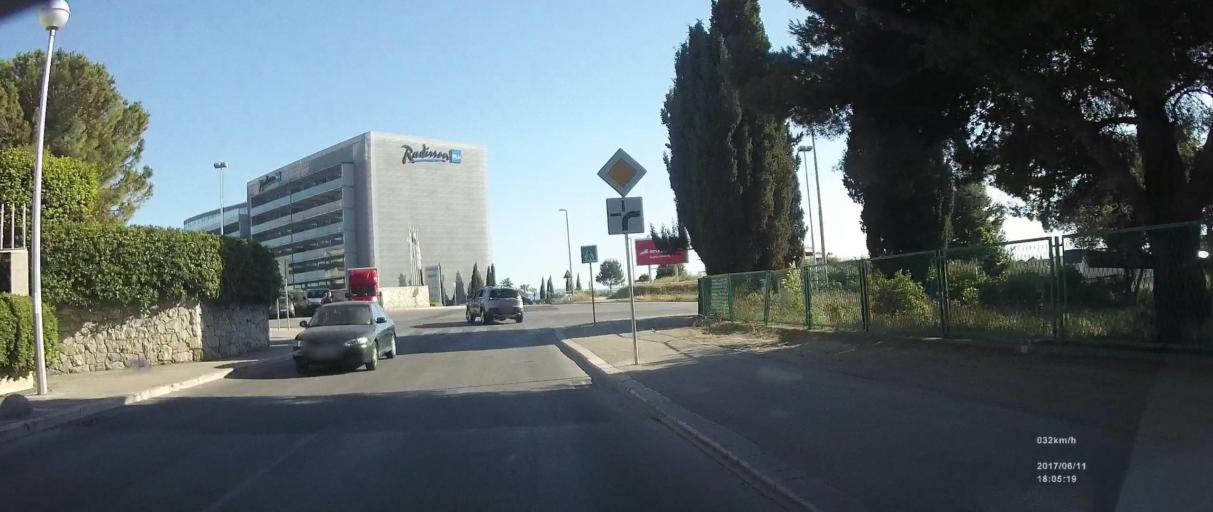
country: HR
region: Splitsko-Dalmatinska
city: Vranjic
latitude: 43.5041
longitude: 16.4703
